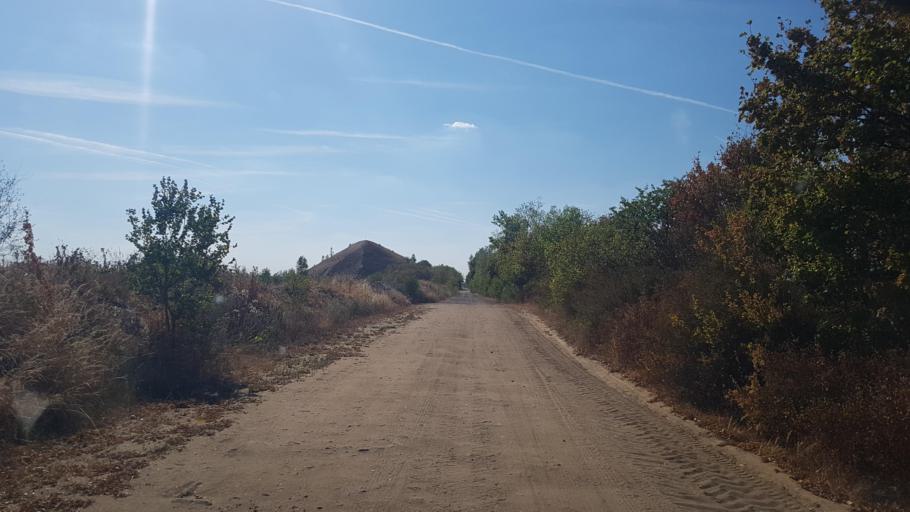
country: DE
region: Brandenburg
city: Muhlberg
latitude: 51.4247
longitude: 13.2837
